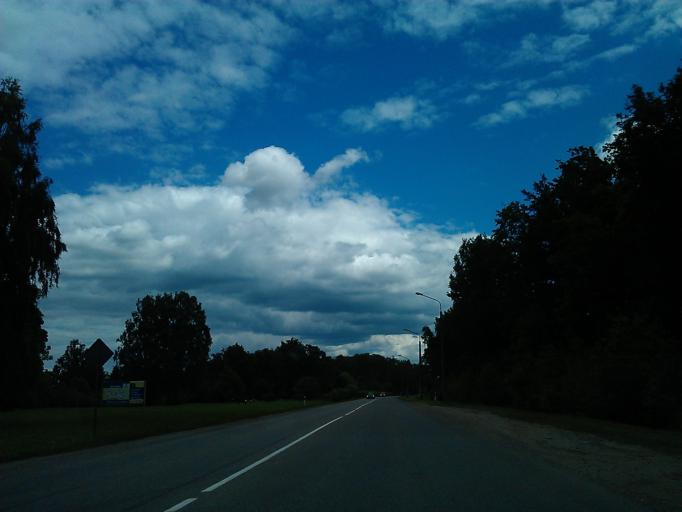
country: LV
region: Jelgava
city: Jelgava
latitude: 56.6302
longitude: 23.7362
